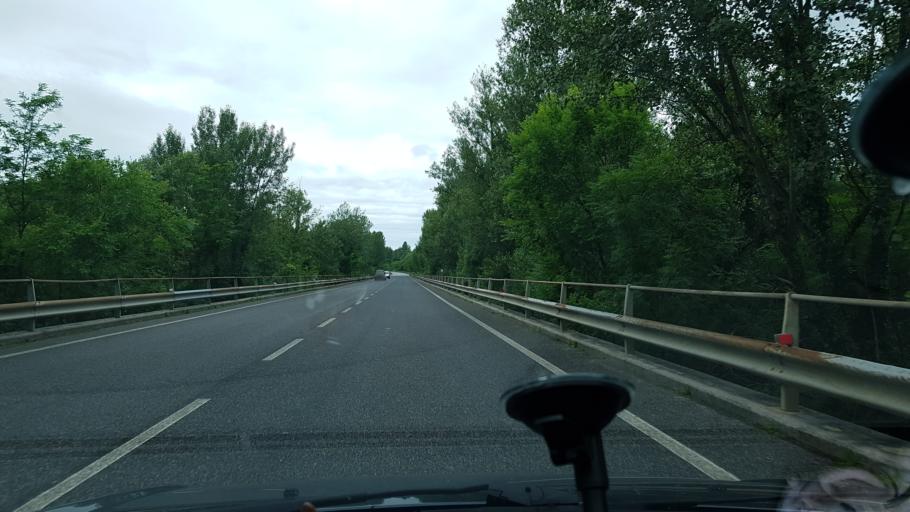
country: IT
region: Friuli Venezia Giulia
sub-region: Provincia di Gorizia
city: Savogna d'Isonzo
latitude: 45.9196
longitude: 13.5871
